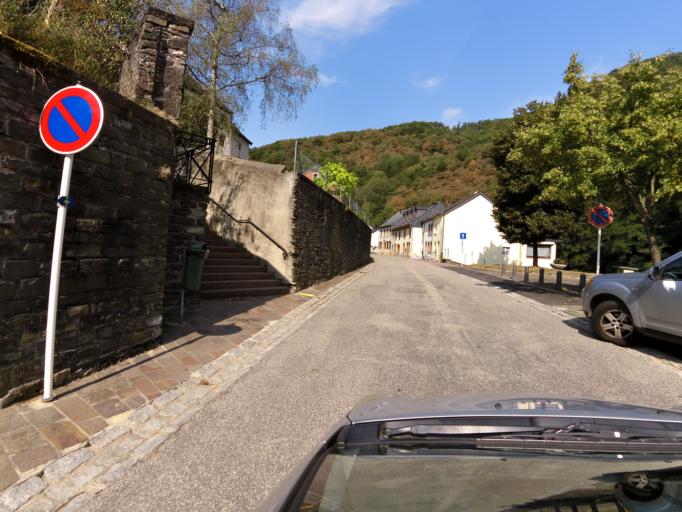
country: LU
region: Diekirch
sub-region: Canton de Wiltz
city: Esch-sur-Sure
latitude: 49.9120
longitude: 5.9360
